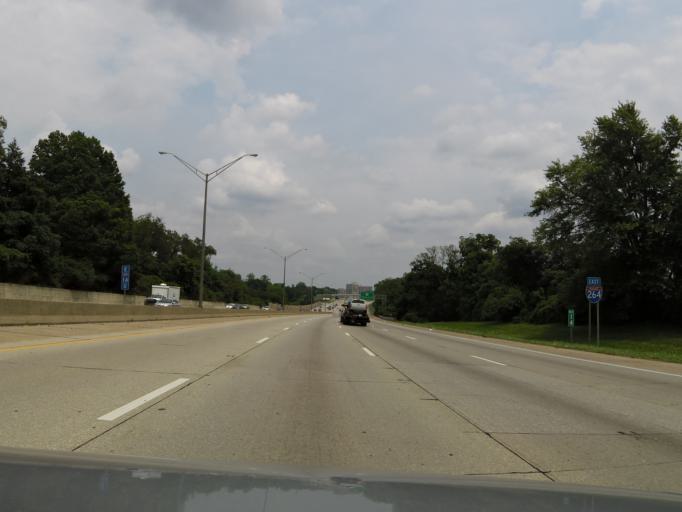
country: US
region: Kentucky
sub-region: Jefferson County
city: Audubon Park
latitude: 38.2000
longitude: -85.6991
